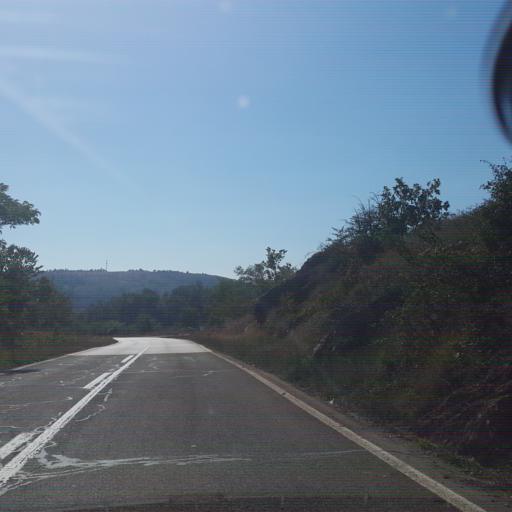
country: RS
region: Central Serbia
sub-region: Nisavski Okrug
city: Svrljig
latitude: 43.4581
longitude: 22.2053
